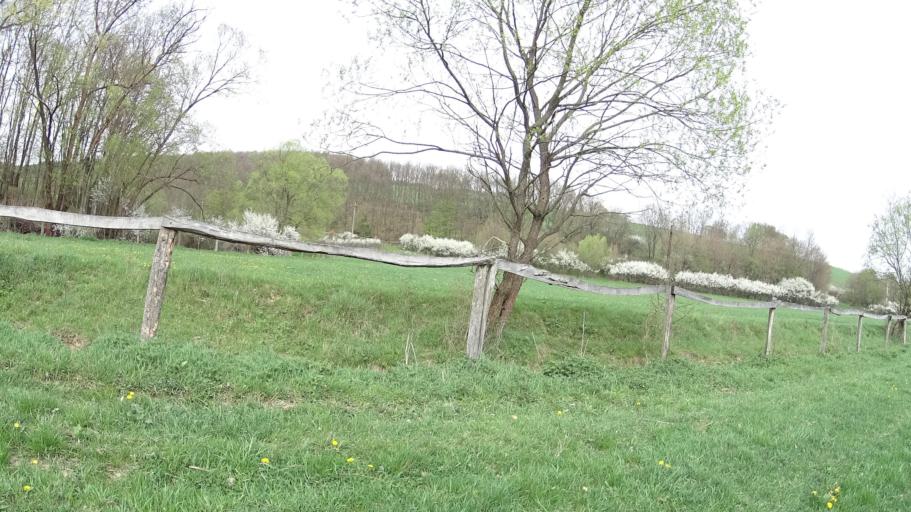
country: HU
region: Pest
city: Veroce
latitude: 47.8779
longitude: 19.0828
